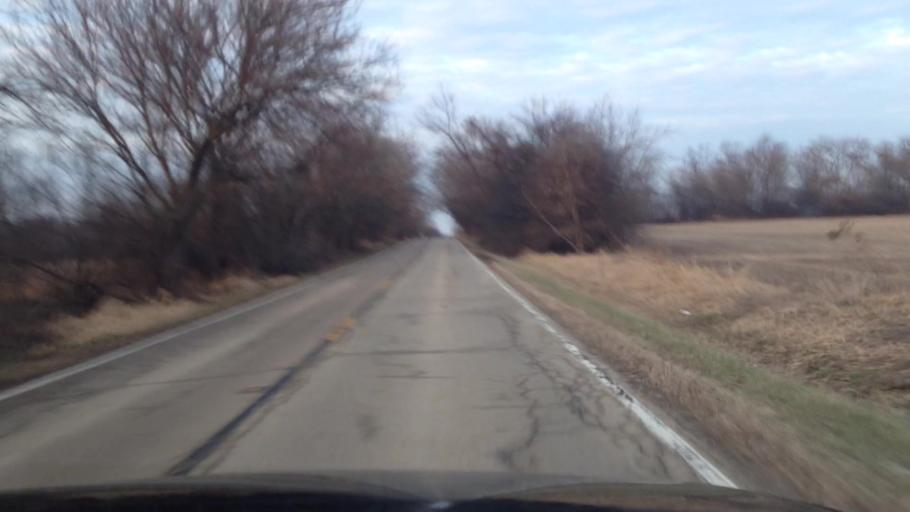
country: US
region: Illinois
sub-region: Cook County
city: Streamwood
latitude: 42.0825
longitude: -88.1946
